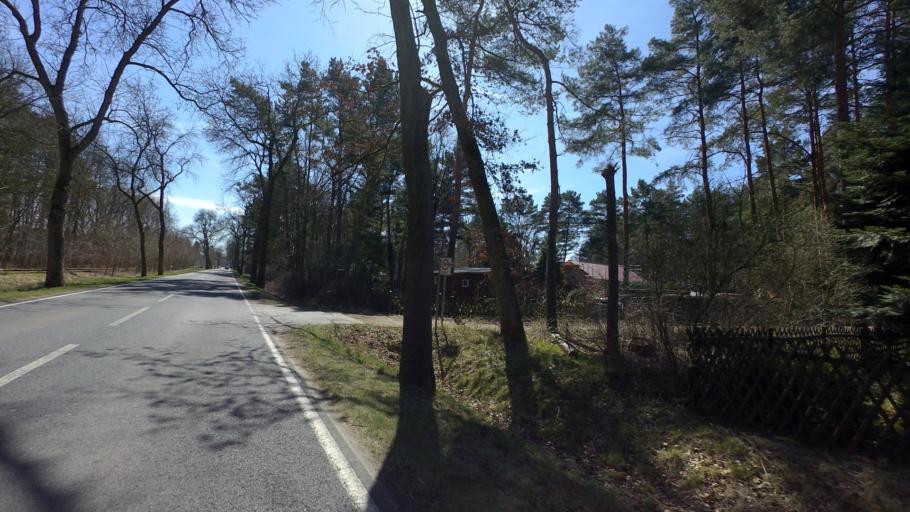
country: DE
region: Brandenburg
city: Mittenwalde
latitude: 52.2234
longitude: 13.5762
